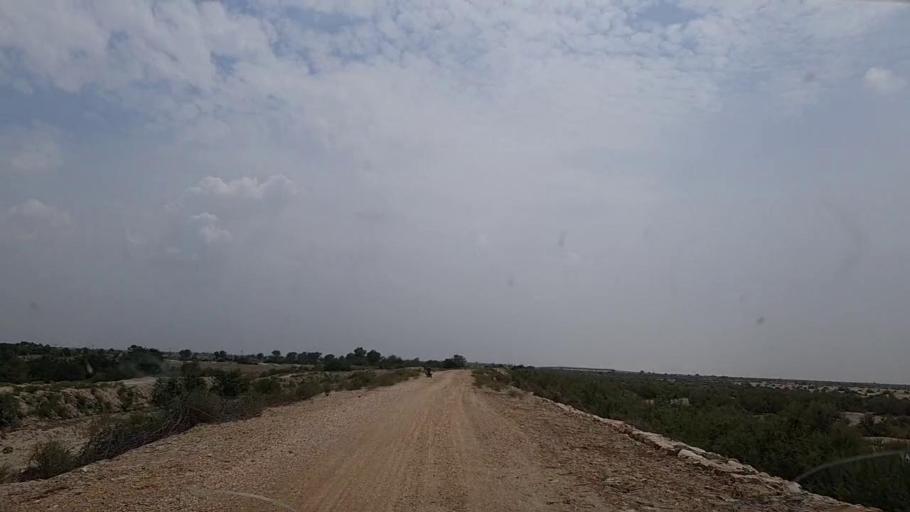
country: PK
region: Sindh
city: Phulji
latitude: 26.8300
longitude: 67.6168
